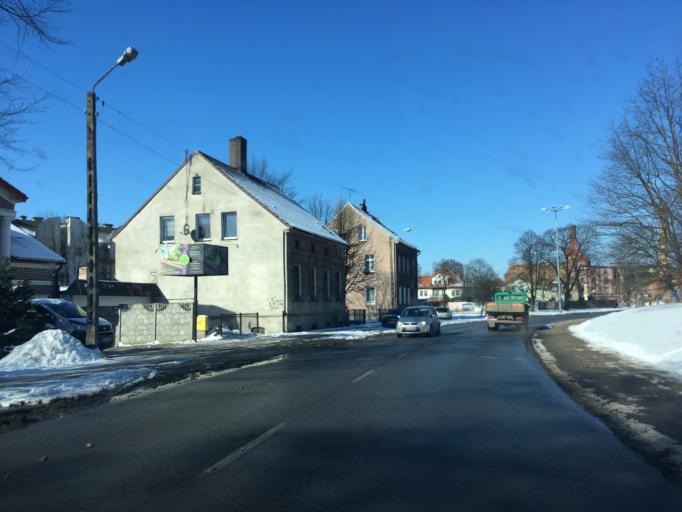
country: PL
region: Pomeranian Voivodeship
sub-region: Slupsk
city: Slupsk
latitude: 54.4698
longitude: 17.0398
